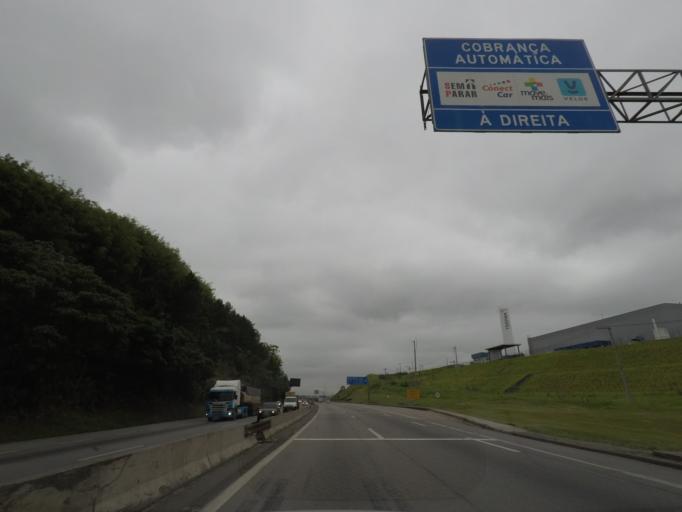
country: BR
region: Sao Paulo
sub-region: Jacarei
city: Jacarei
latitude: -23.2995
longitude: -46.0129
